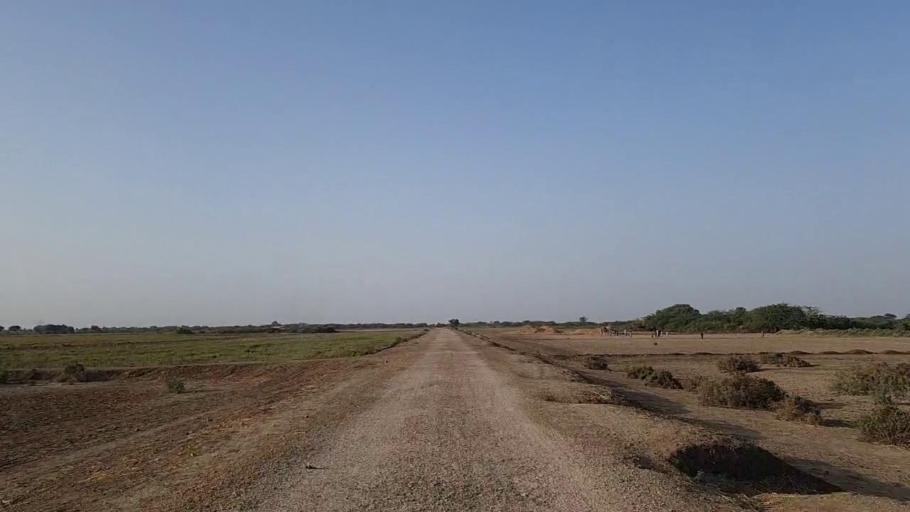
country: PK
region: Sindh
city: Jati
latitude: 24.3777
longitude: 68.1479
